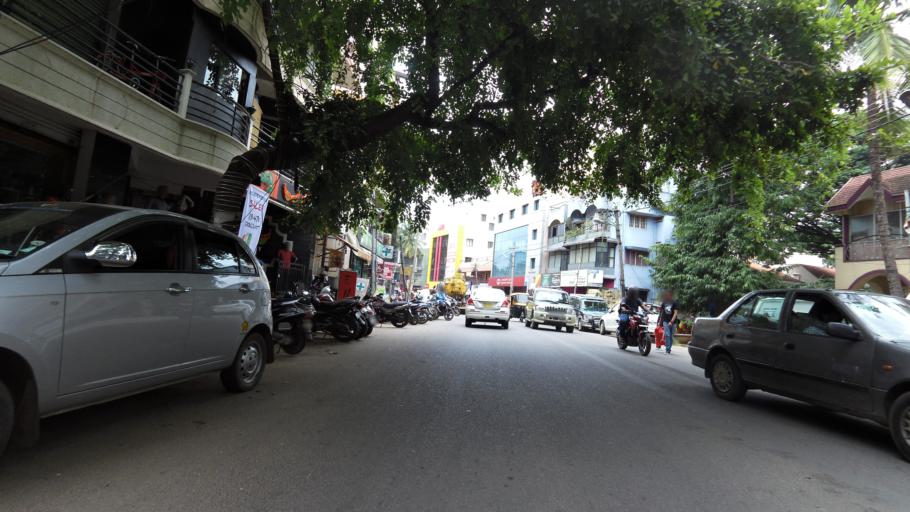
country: IN
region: Karnataka
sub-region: Bangalore Urban
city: Bangalore
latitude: 12.9745
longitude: 77.6360
